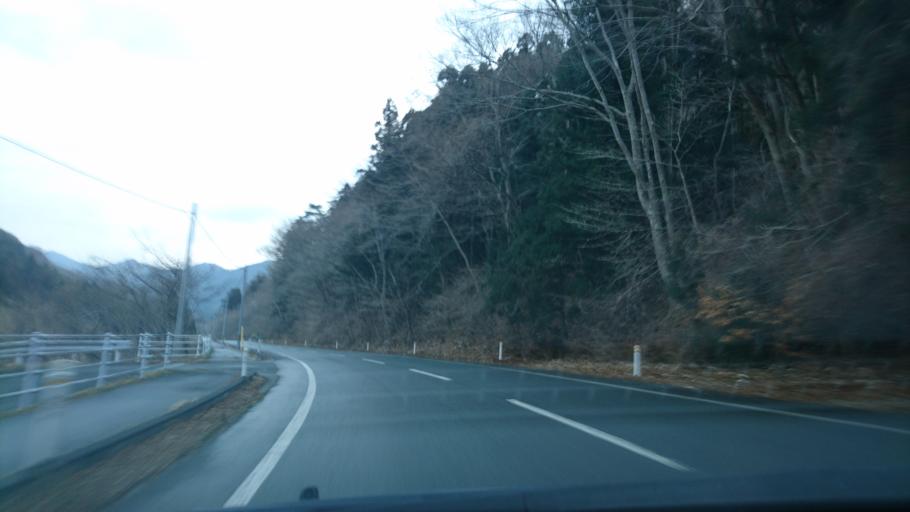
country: JP
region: Iwate
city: Ofunato
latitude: 39.0117
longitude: 141.5461
